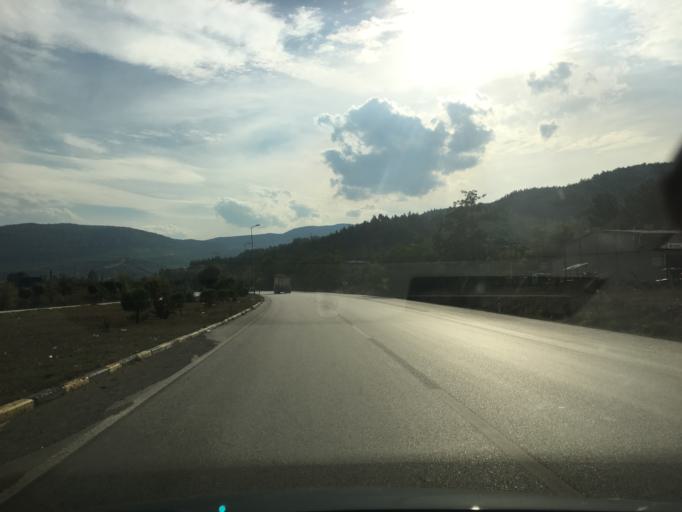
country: TR
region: Karabuk
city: Karabuk
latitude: 41.1191
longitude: 32.6745
